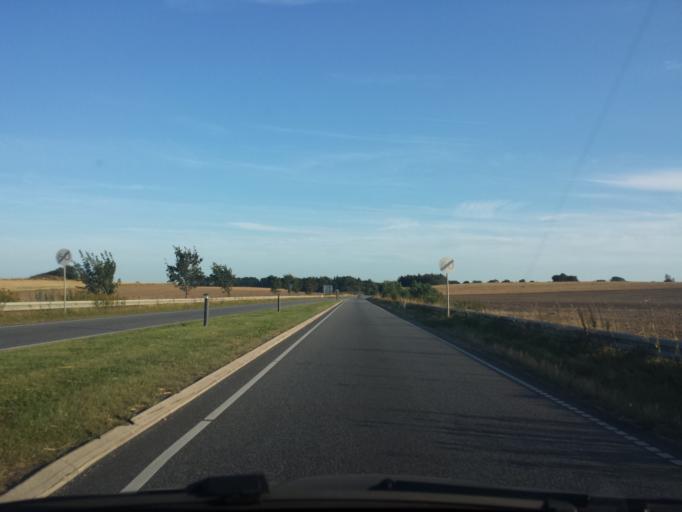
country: DK
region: Capital Region
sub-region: Frederikssund Kommune
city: Frederikssund
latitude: 55.8349
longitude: 12.1013
